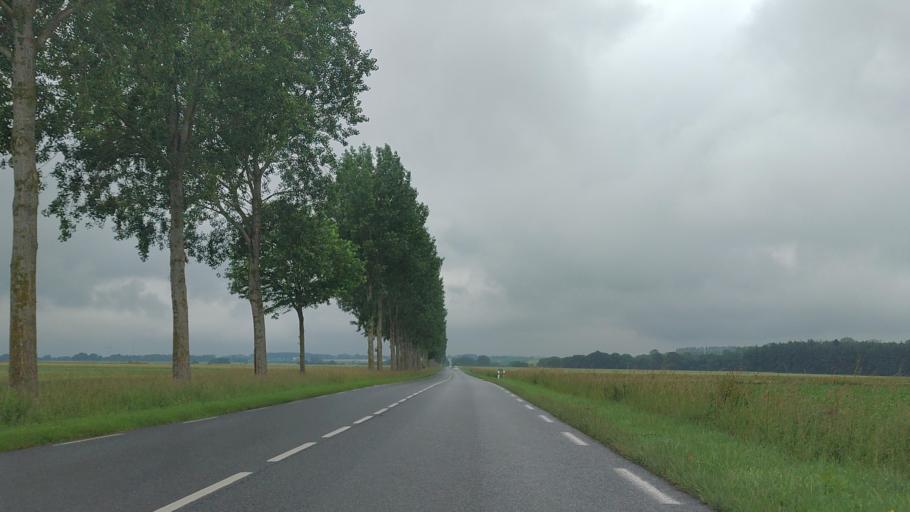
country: FR
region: Picardie
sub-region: Departement de la Somme
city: Chepy
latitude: 50.0913
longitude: 1.6976
